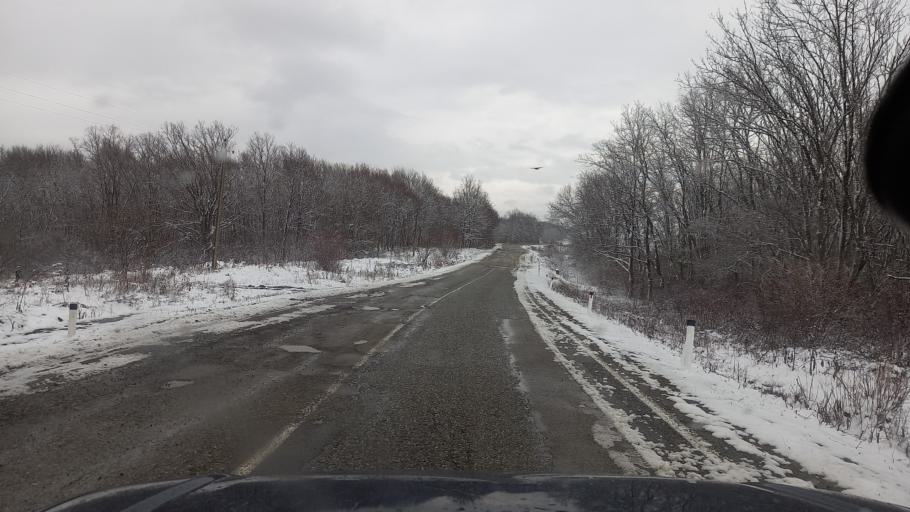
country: RU
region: Adygeya
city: Abadzekhskaya
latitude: 44.3472
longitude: 40.3598
